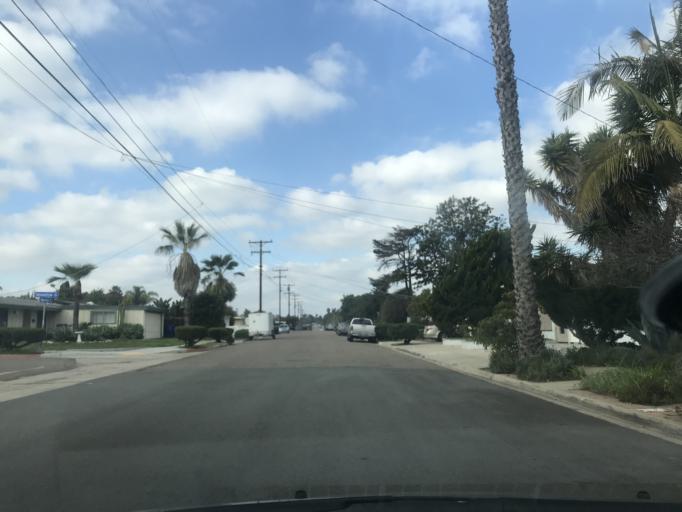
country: US
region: California
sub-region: San Diego County
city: San Diego
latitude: 32.7963
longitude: -117.1242
